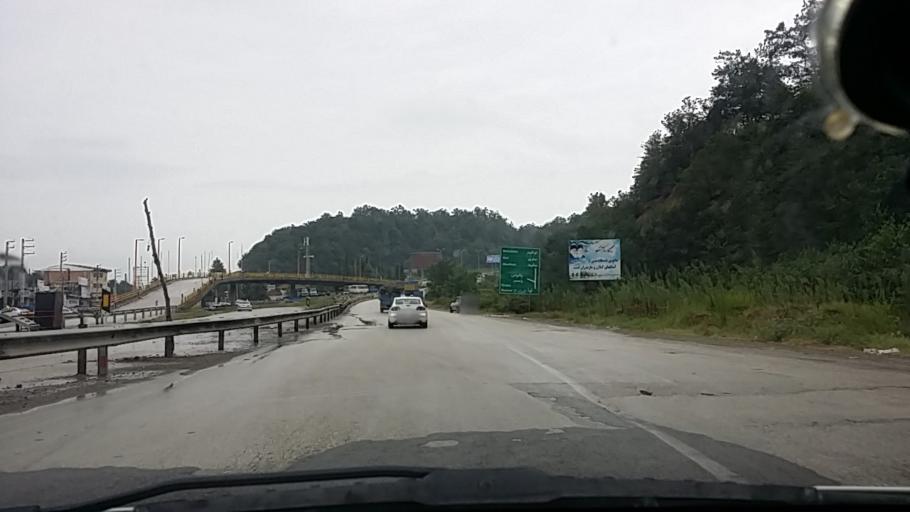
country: IR
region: Mazandaran
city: Chalus
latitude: 36.6334
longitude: 51.4098
